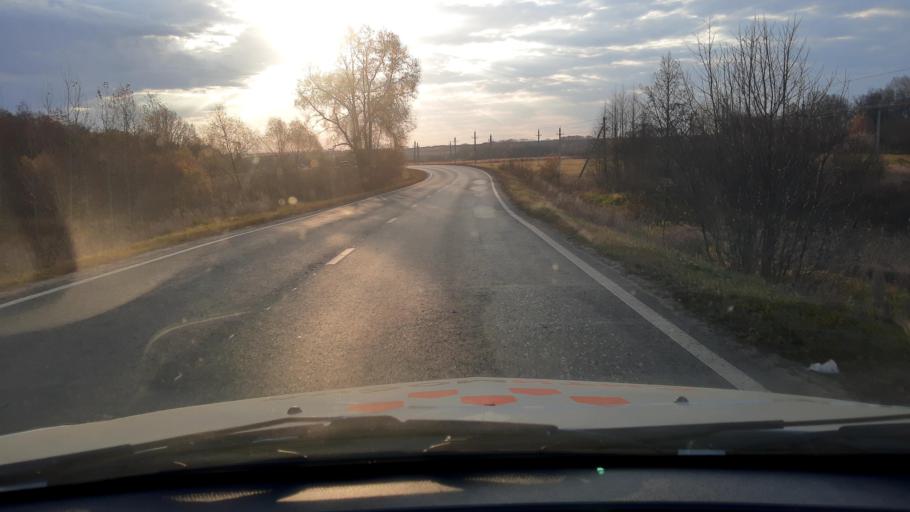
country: RU
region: Bashkortostan
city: Iglino
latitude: 54.7437
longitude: 56.2178
